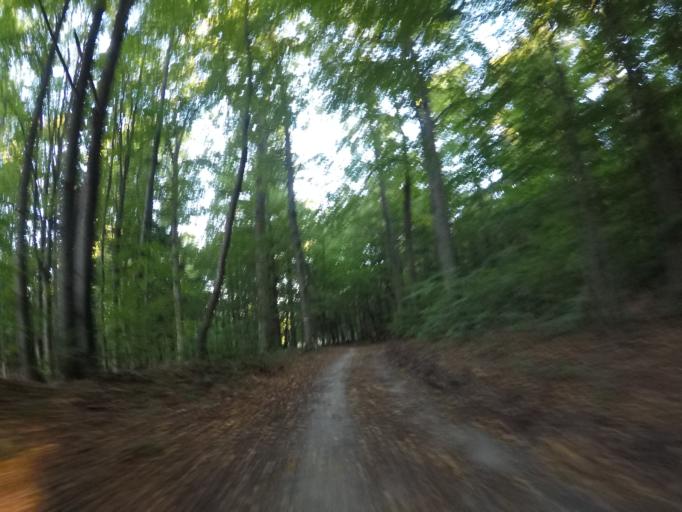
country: SK
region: Kosicky
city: Kosice
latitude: 48.7498
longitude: 21.1693
